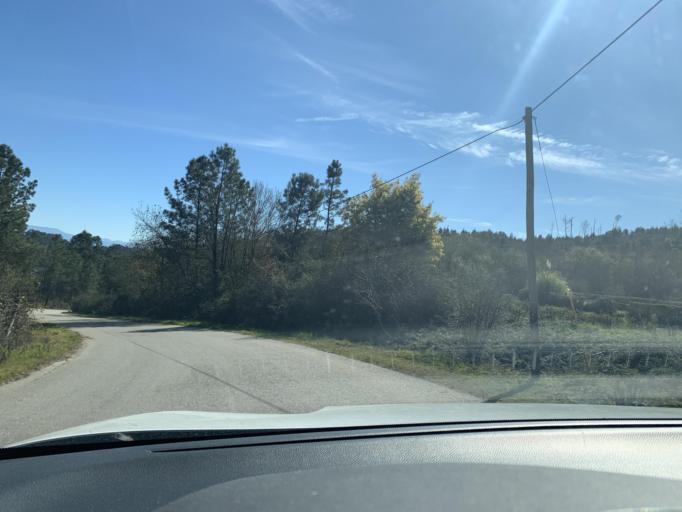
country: PT
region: Viseu
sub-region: Concelho de Tondela
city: Tondela
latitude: 40.6045
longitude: -8.0326
